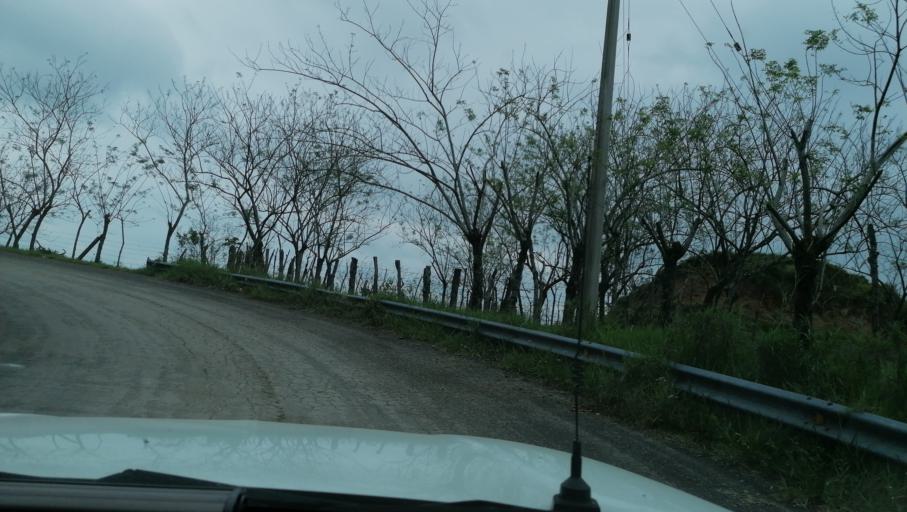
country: MX
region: Chiapas
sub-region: Francisco Leon
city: San Miguel la Sardina
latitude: 17.2722
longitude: -93.2659
